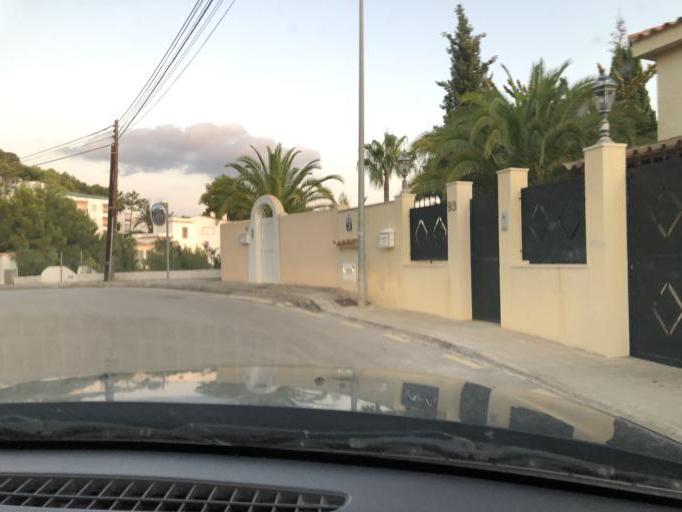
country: ES
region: Balearic Islands
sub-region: Illes Balears
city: Santa Ponsa
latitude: 39.5278
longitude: 2.4704
